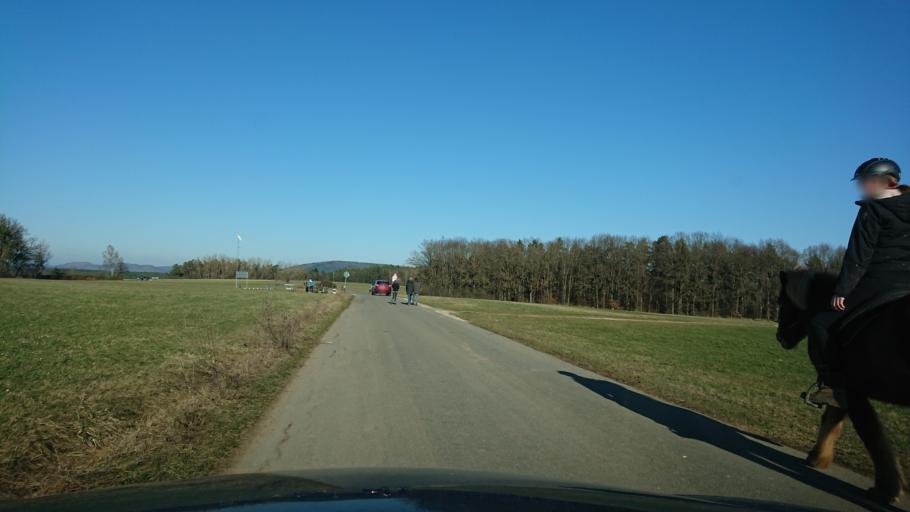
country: DE
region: Bavaria
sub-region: Regierungsbezirk Mittelfranken
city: Marloffstein
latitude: 49.6233
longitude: 11.0785
